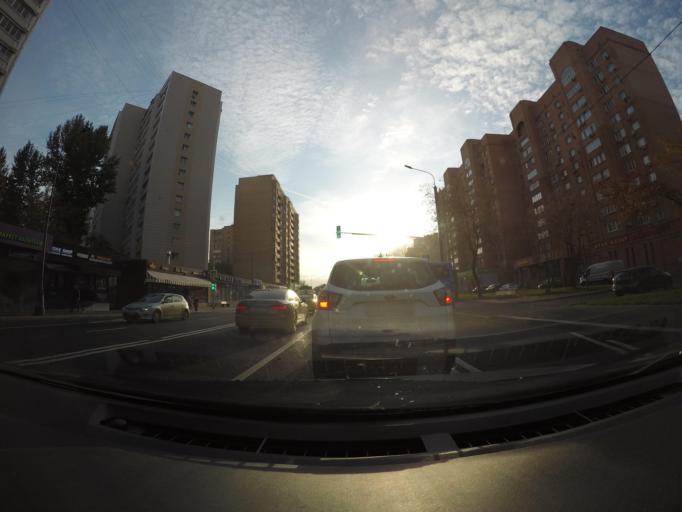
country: RU
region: Moscow
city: Lefortovo
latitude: 55.7762
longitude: 37.6864
